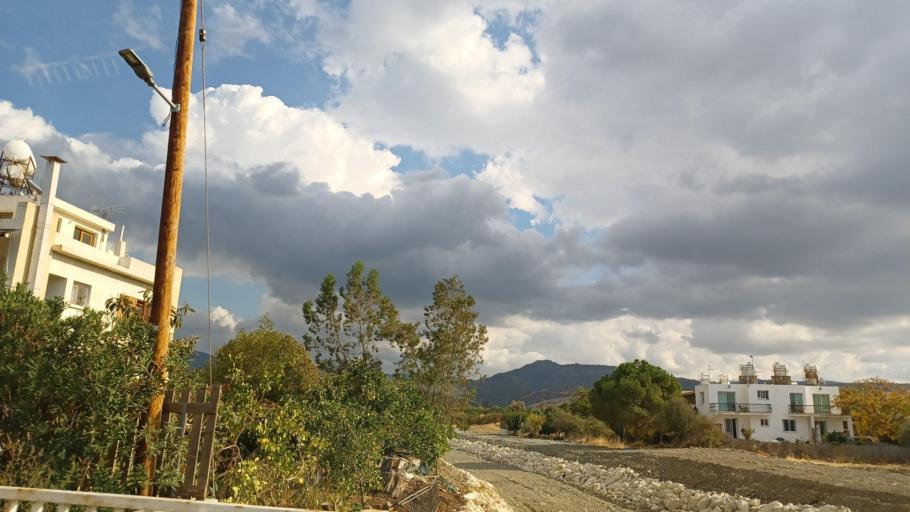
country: CY
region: Pafos
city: Polis
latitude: 35.0656
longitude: 32.4686
